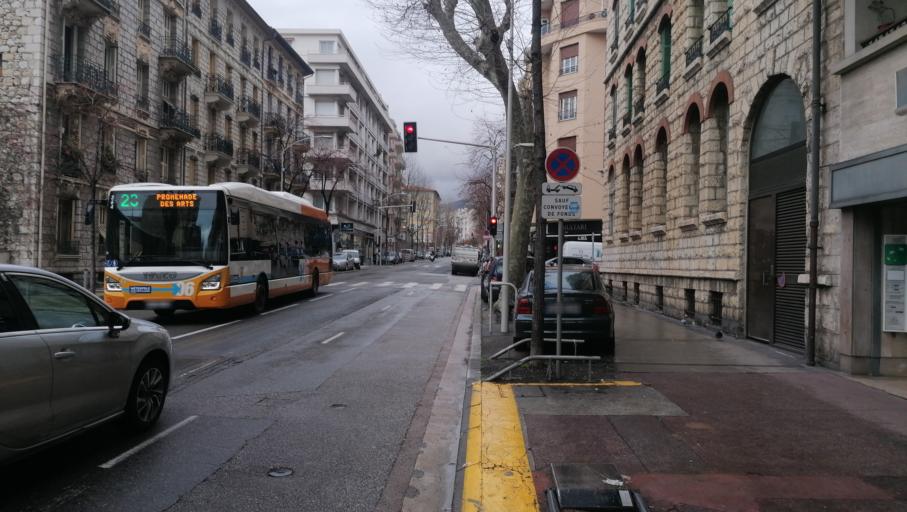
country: FR
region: Provence-Alpes-Cote d'Azur
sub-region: Departement des Alpes-Maritimes
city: Nice
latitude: 43.7076
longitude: 7.2560
